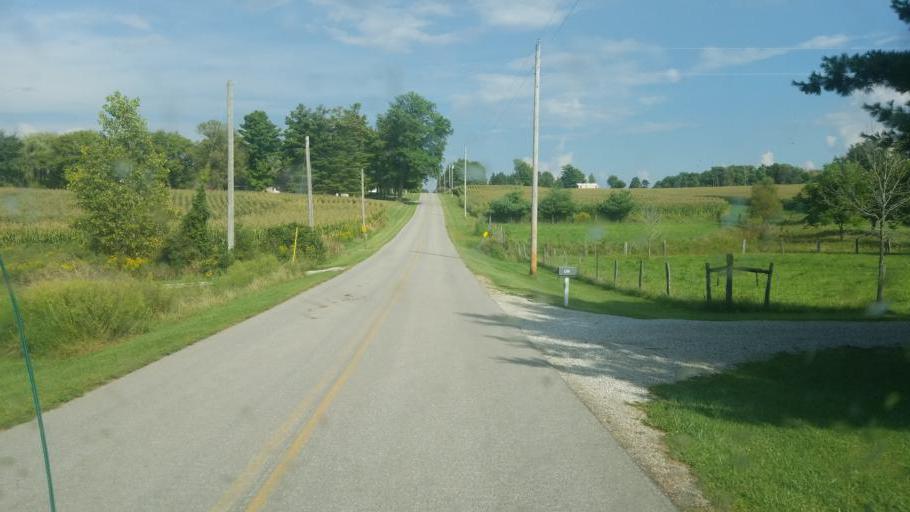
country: US
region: Ohio
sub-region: Huron County
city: Plymouth
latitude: 41.0067
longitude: -82.6216
